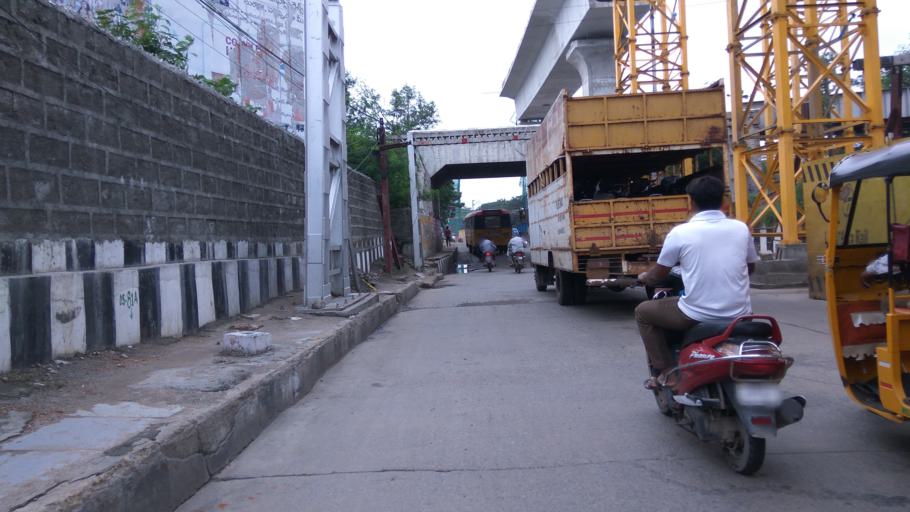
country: IN
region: Telangana
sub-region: Hyderabad
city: Malkajgiri
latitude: 17.4348
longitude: 78.5132
